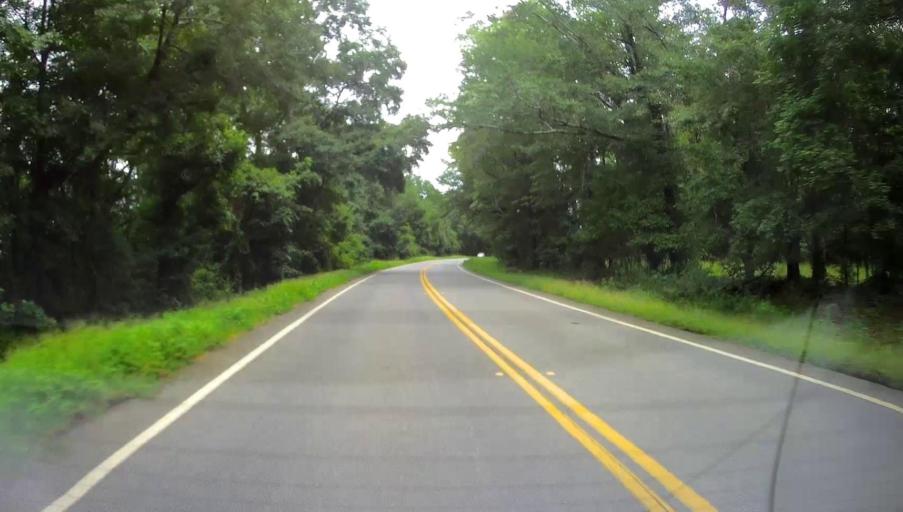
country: US
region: Georgia
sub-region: Schley County
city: Ellaville
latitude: 32.2527
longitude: -84.3906
